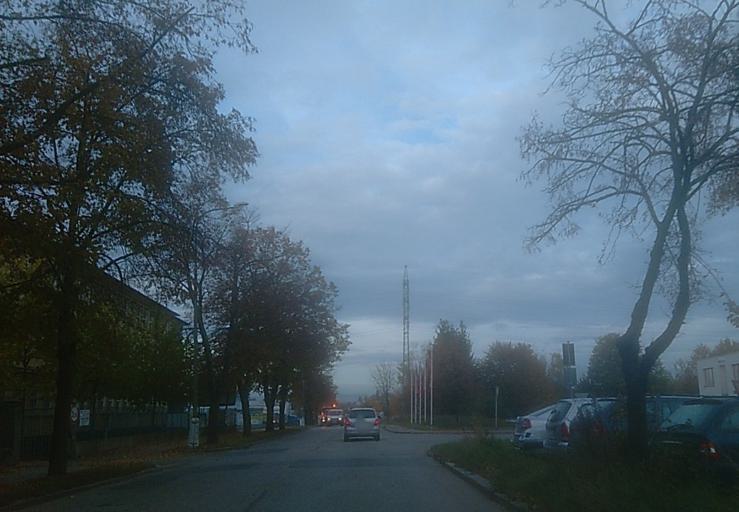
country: CZ
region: Jihocesky
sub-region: Okres Ceske Budejovice
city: Ceske Budejovice
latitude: 48.9756
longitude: 14.5014
